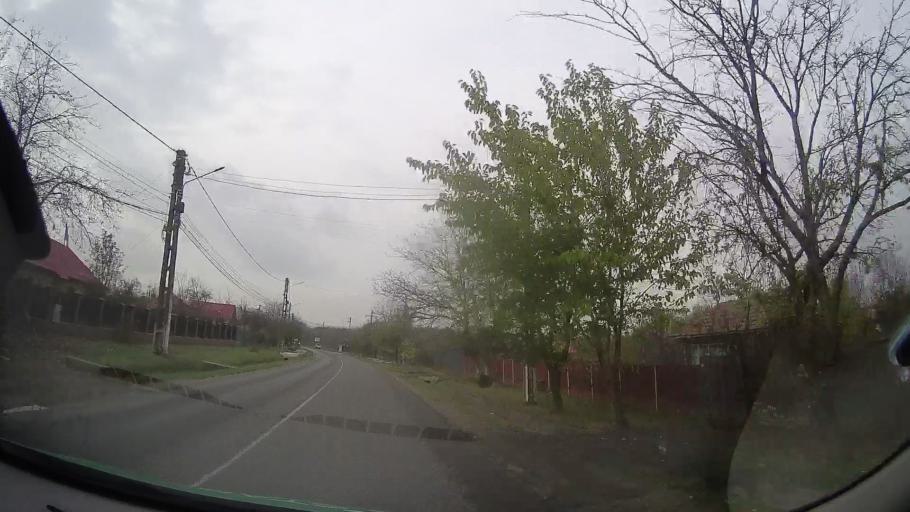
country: RO
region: Ilfov
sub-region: Comuna Gruiu
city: Gruiu
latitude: 44.7229
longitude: 26.2154
